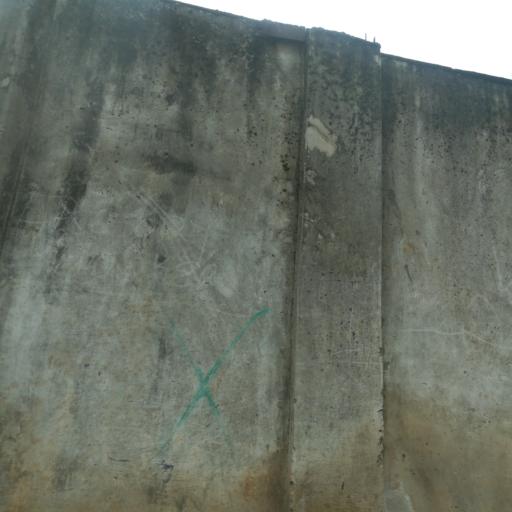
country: NG
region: Lagos
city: Agege
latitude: 6.6027
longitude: 3.2938
